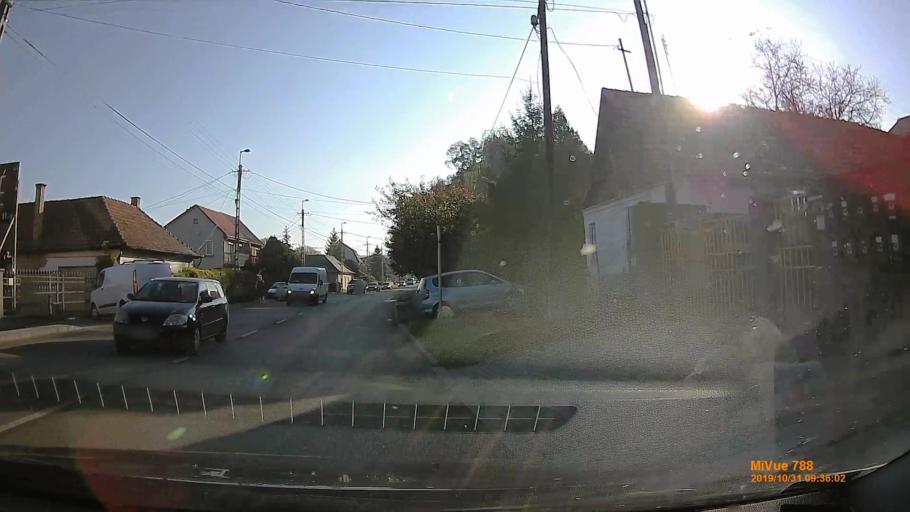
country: HU
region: Pest
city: Pecel
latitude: 47.4913
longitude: 19.3242
